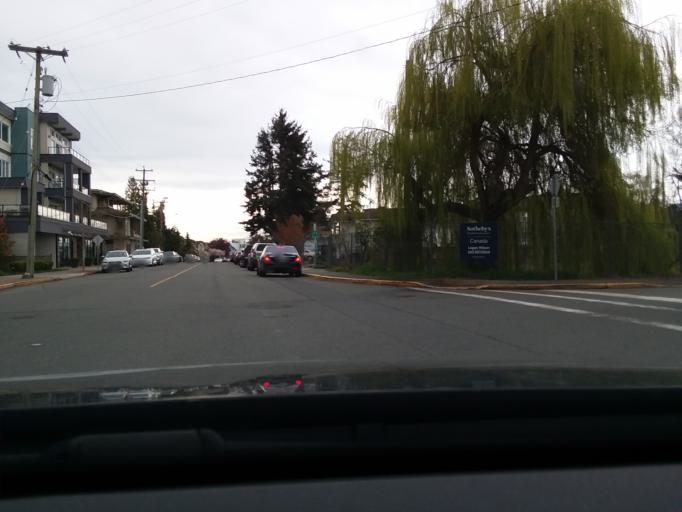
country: CA
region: British Columbia
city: North Saanich
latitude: 48.6477
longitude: -123.3954
